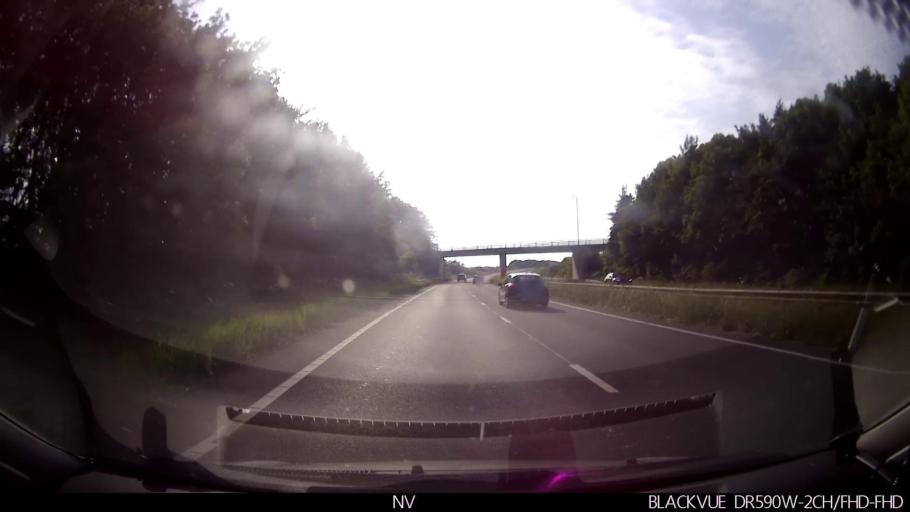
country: GB
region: England
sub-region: North Yorkshire
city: Malton
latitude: 54.1422
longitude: -0.7479
